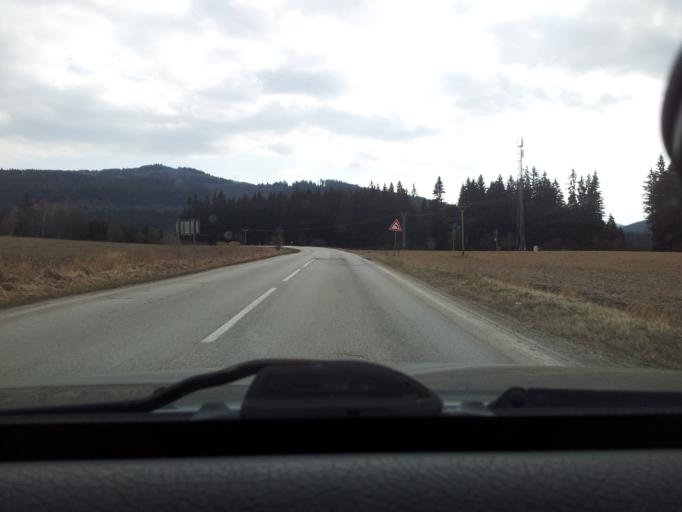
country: SK
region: Banskobystricky
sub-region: Okres Ziar nad Hronom
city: Kremnica
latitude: 48.7834
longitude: 18.8760
